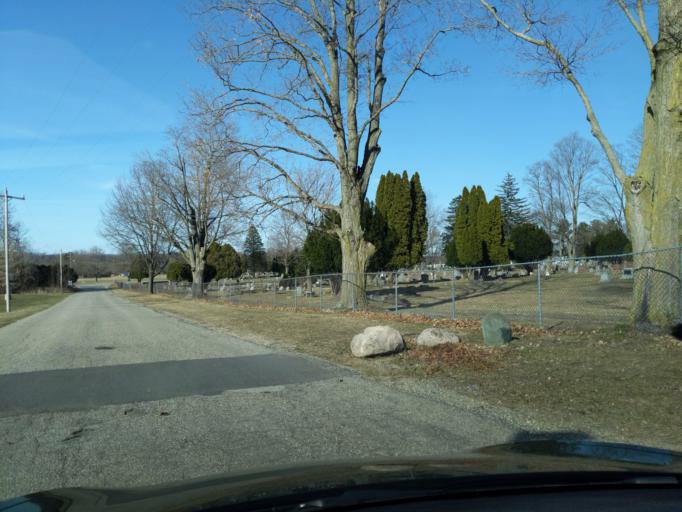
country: US
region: Michigan
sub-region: Ionia County
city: Saranac
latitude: 42.9281
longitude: -85.2002
